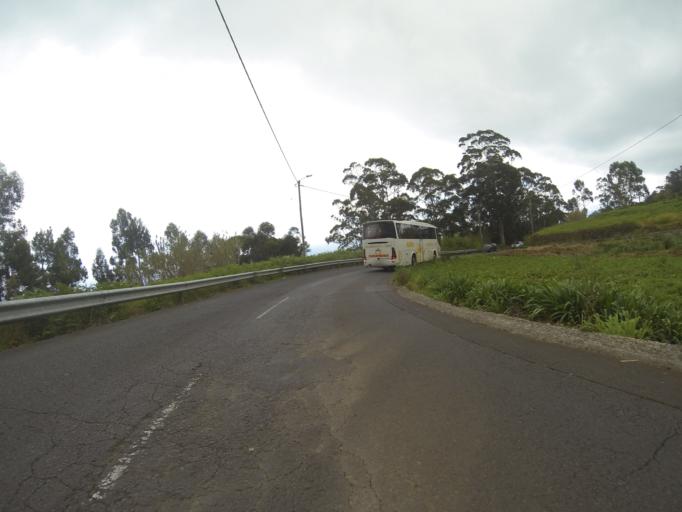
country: PT
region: Madeira
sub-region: Porto Moniz
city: Porto Moniz
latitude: 32.8599
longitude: -17.1746
